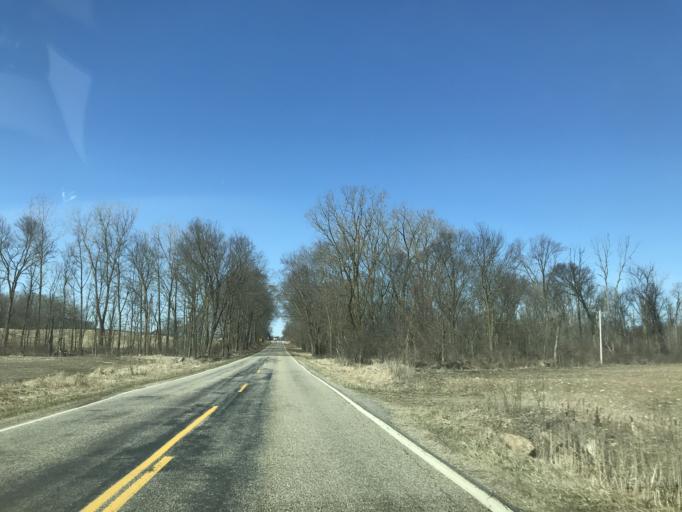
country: US
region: Michigan
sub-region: Hillsdale County
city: Litchfield
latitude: 41.9856
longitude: -84.7627
